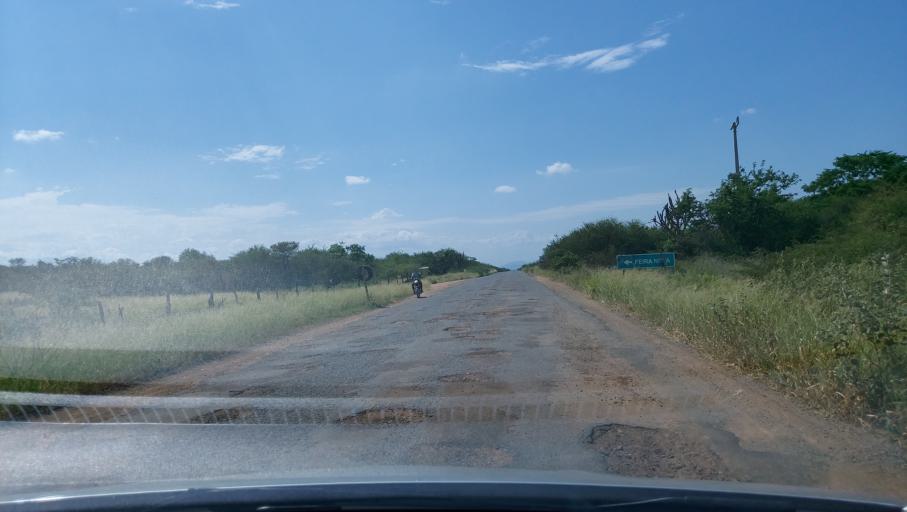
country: BR
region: Bahia
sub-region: Oliveira Dos Brejinhos
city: Beira Rio
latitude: -12.1635
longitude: -42.5487
